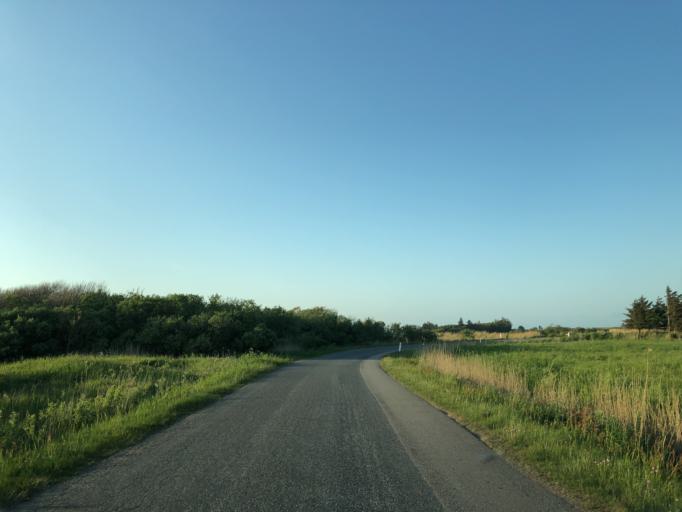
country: DK
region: Central Jutland
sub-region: Ringkobing-Skjern Kommune
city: Ringkobing
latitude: 56.2025
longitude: 8.1594
